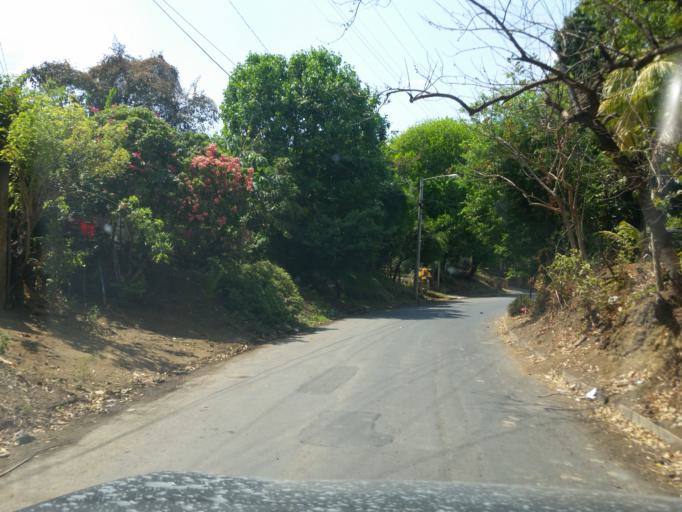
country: NI
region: Managua
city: Managua
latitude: 12.0833
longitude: -86.2186
